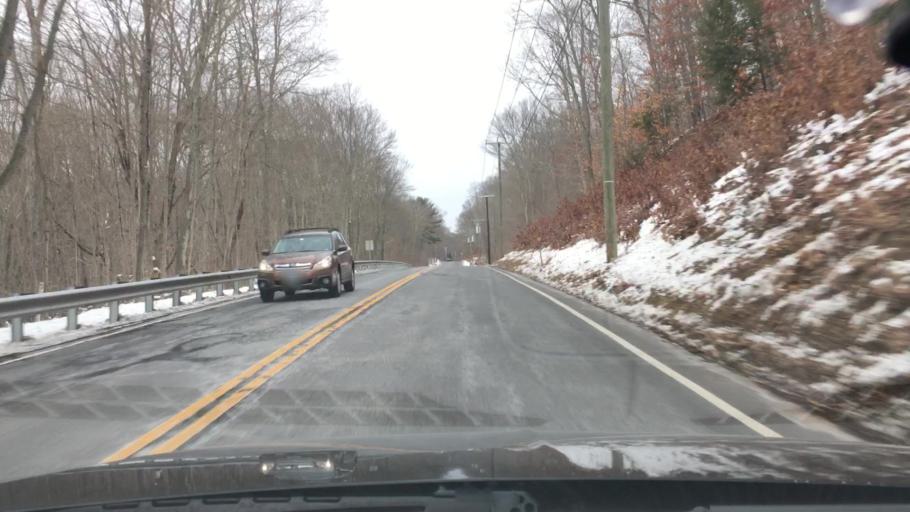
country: US
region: Connecticut
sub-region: Tolland County
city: Tolland
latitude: 41.8392
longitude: -72.3167
